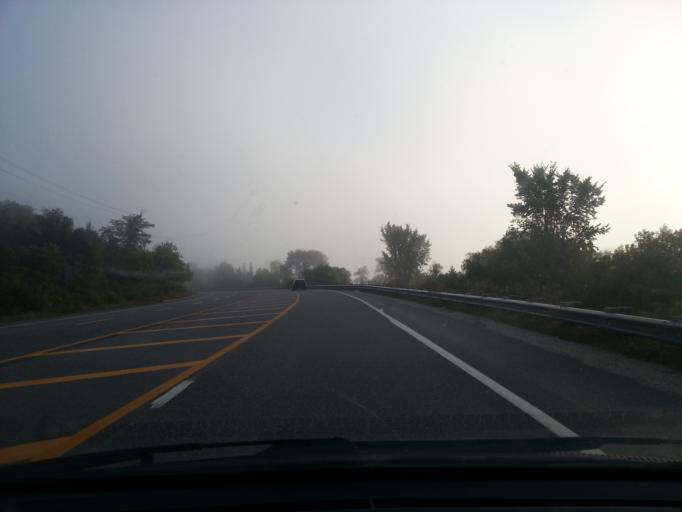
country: CA
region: Quebec
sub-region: Outaouais
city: Wakefield
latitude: 45.7069
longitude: -75.9221
